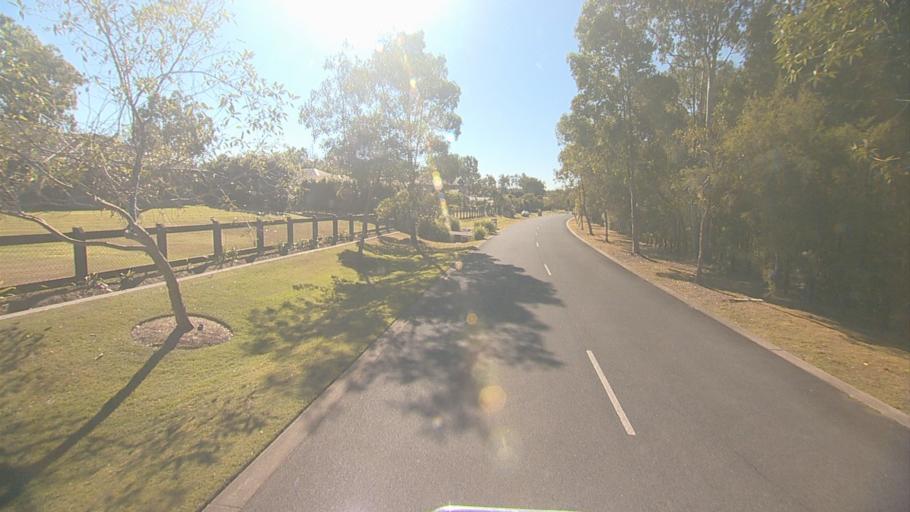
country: AU
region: Queensland
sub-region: Logan
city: North Maclean
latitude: -27.7566
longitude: 152.9610
